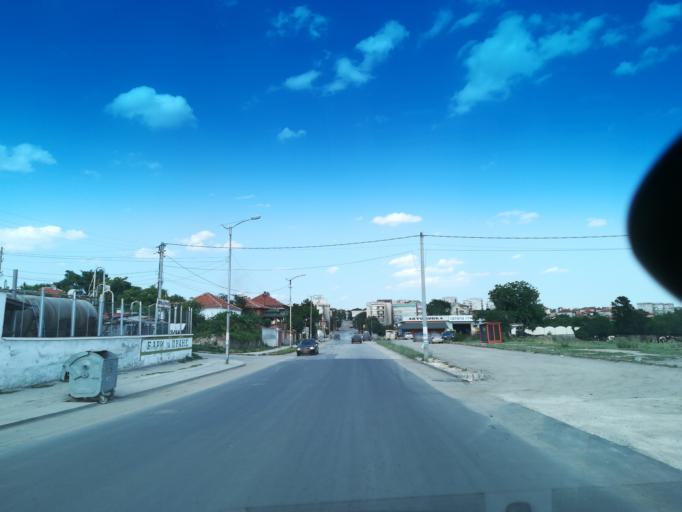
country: BG
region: Stara Zagora
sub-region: Obshtina Chirpan
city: Chirpan
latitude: 42.1975
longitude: 25.3178
